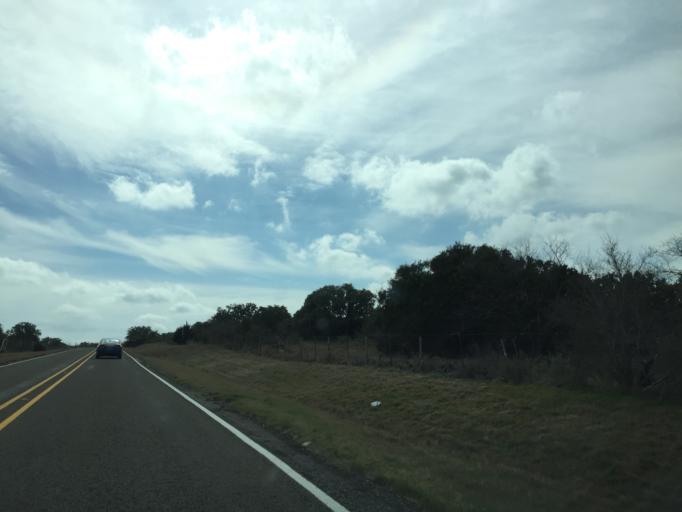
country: US
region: Texas
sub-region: Burnet County
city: Granite Shoals
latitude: 30.5018
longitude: -98.4409
